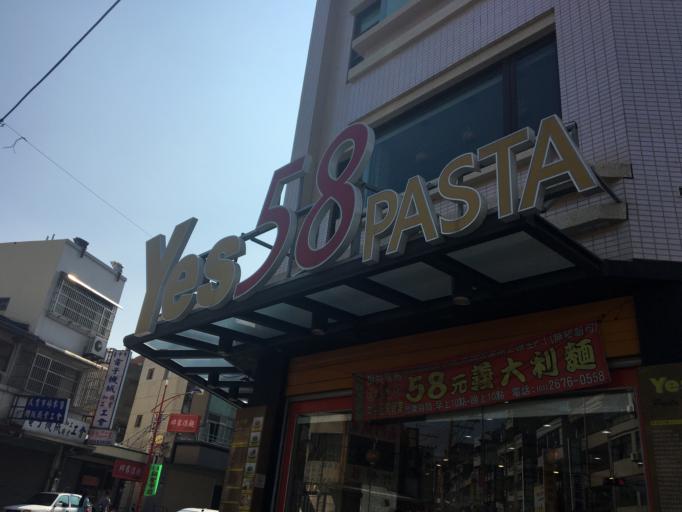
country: TW
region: Taiwan
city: Fengyuan
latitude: 24.3442
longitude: 120.6217
